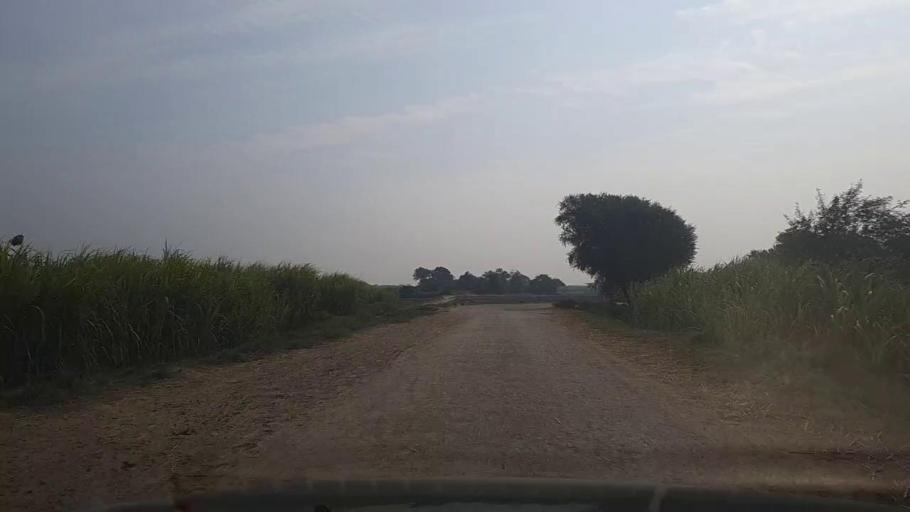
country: PK
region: Sindh
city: Bulri
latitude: 25.0233
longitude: 68.2986
